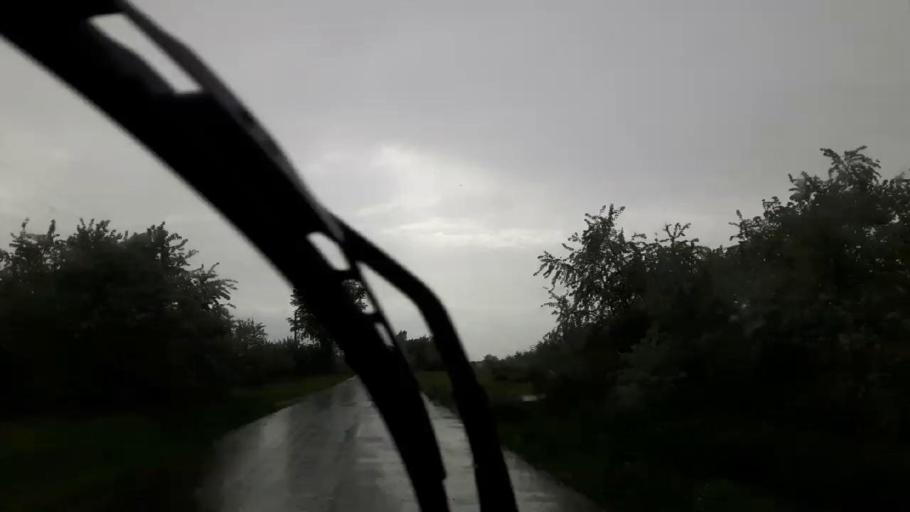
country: GE
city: Agara
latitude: 42.0141
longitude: 43.8011
